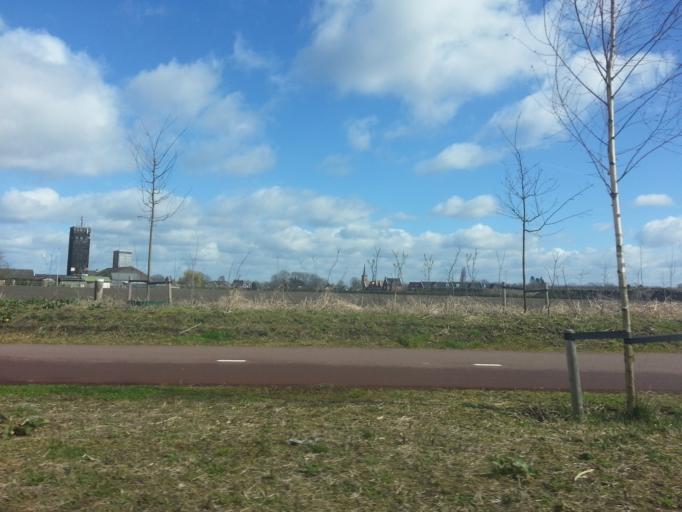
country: NL
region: North Brabant
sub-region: Gemeente Veldhoven
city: Oerle
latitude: 51.4169
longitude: 5.3630
